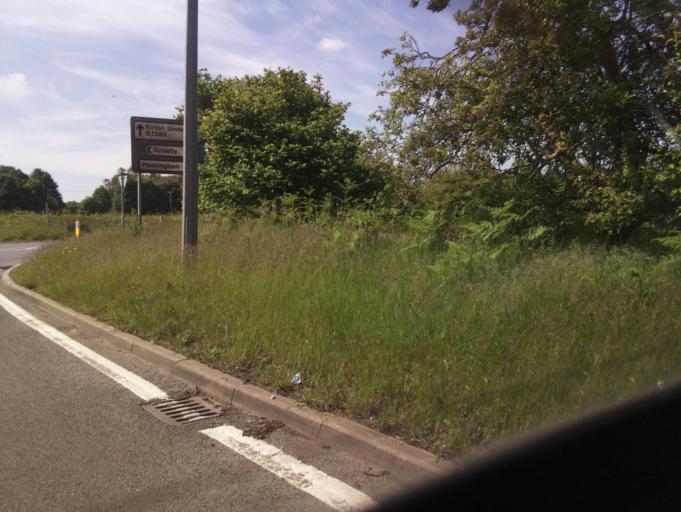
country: GB
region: England
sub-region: North Lincolnshire
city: Manton
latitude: 53.5329
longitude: -0.5773
